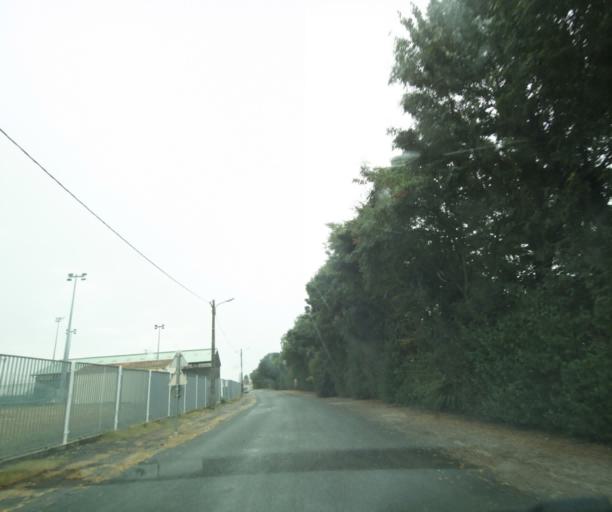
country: FR
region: Poitou-Charentes
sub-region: Departement de la Charente-Maritime
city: Tonnay-Charente
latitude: 45.9443
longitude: -0.9087
